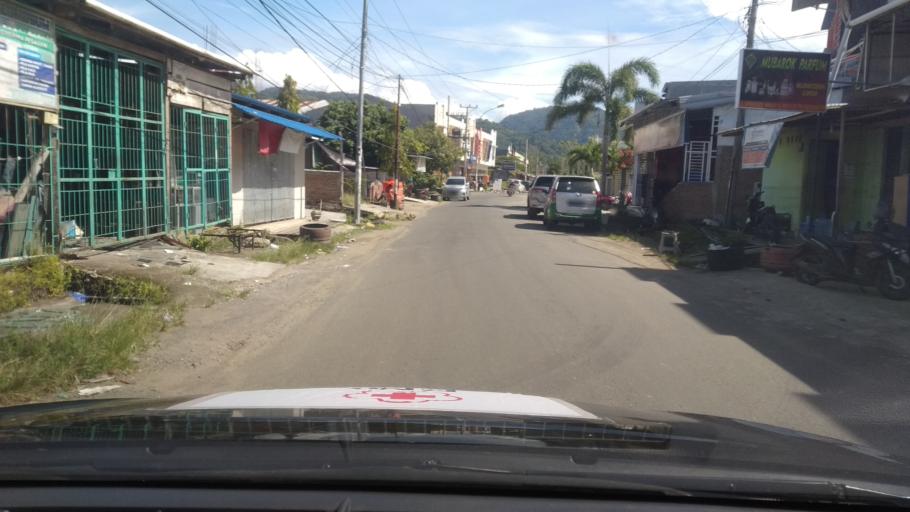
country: ID
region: Sulawesi Barat
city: Mamuju
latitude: -2.6829
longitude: 118.8756
